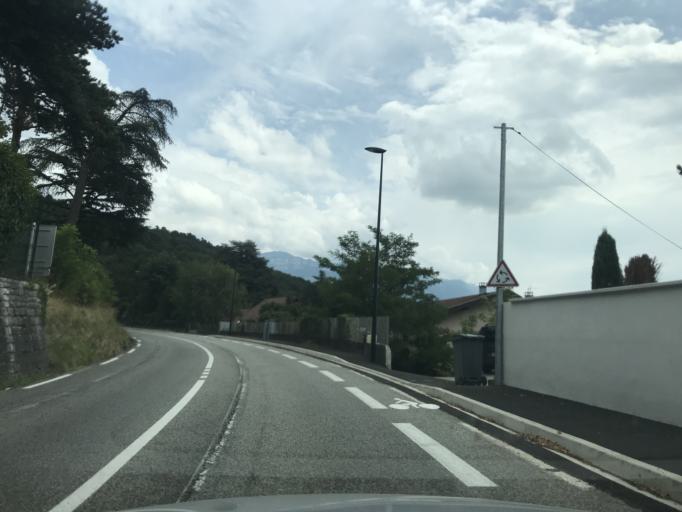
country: FR
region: Rhone-Alpes
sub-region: Departement de la Savoie
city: Brison-Saint-Innocent
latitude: 45.7136
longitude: 5.8912
